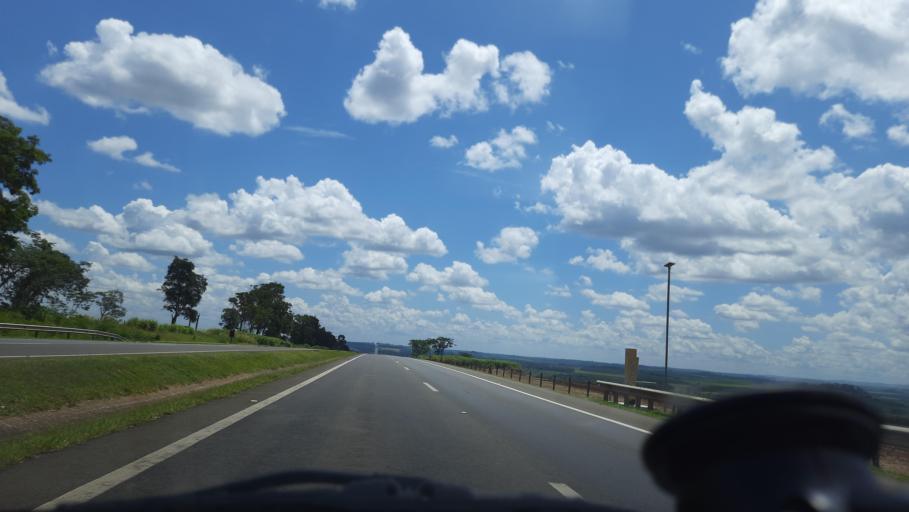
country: BR
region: Sao Paulo
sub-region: Aguai
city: Aguai
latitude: -22.0255
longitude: -47.0337
